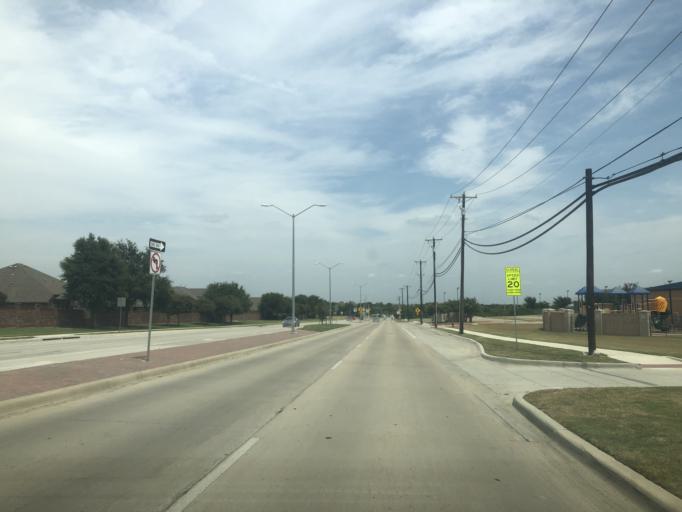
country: US
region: Texas
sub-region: Tarrant County
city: Saginaw
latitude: 32.8837
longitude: -97.3496
